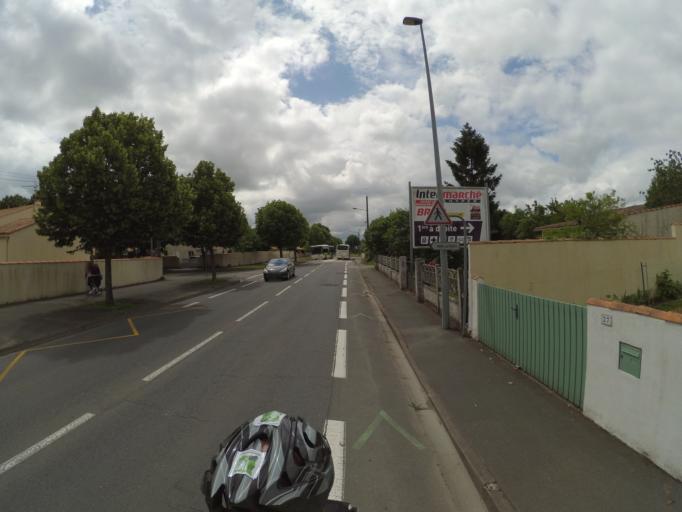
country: FR
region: Poitou-Charentes
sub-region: Departement de la Charente-Maritime
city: Rochefort
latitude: 45.9563
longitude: -0.9692
